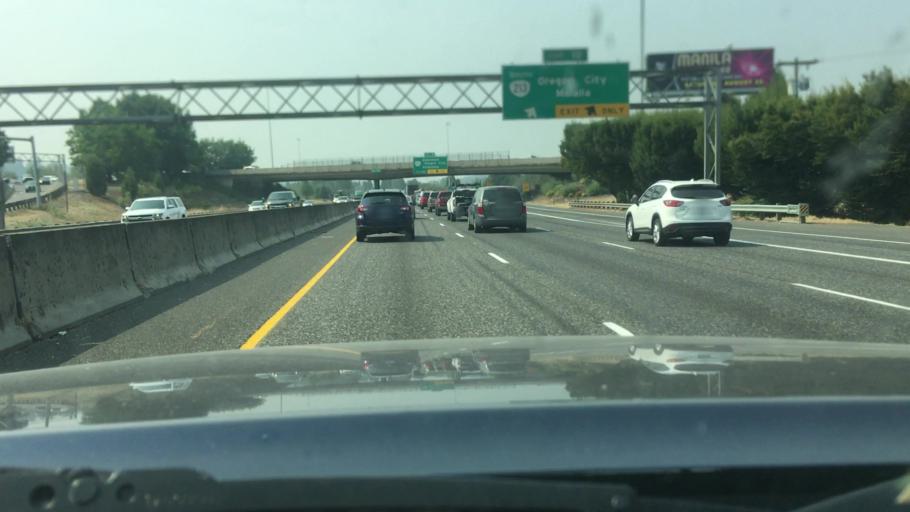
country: US
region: Oregon
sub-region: Clackamas County
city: Gladstone
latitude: 45.3762
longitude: -122.5854
